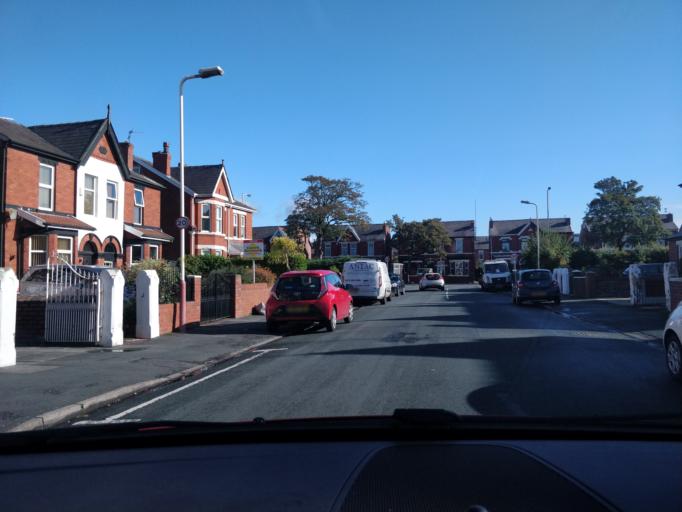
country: GB
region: England
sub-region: Sefton
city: Southport
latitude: 53.6440
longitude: -2.9762
